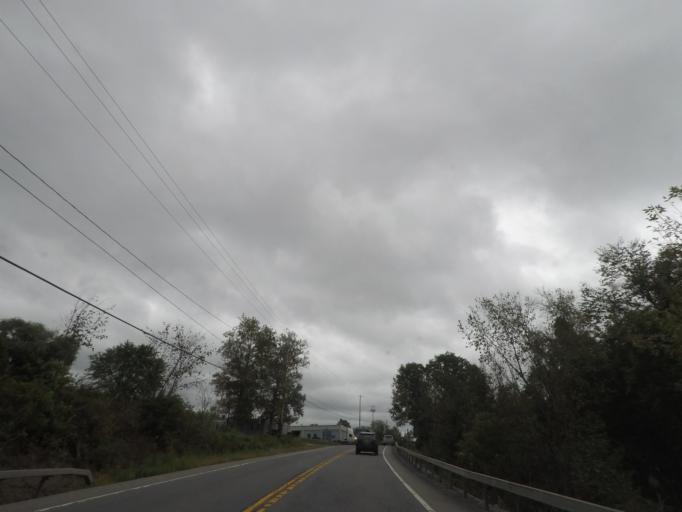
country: US
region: New York
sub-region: Saratoga County
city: Mechanicville
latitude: 42.9186
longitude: -73.7138
